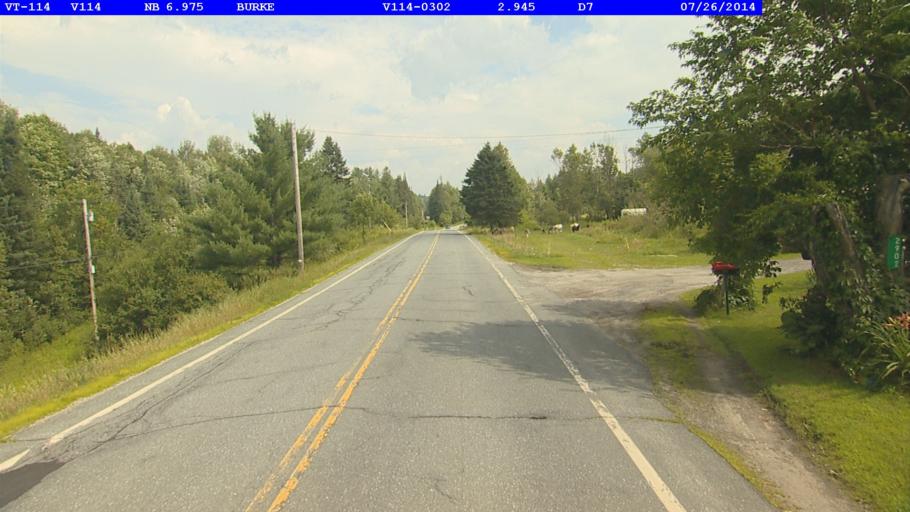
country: US
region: Vermont
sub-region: Caledonia County
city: Lyndonville
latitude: 44.6122
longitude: -71.9102
